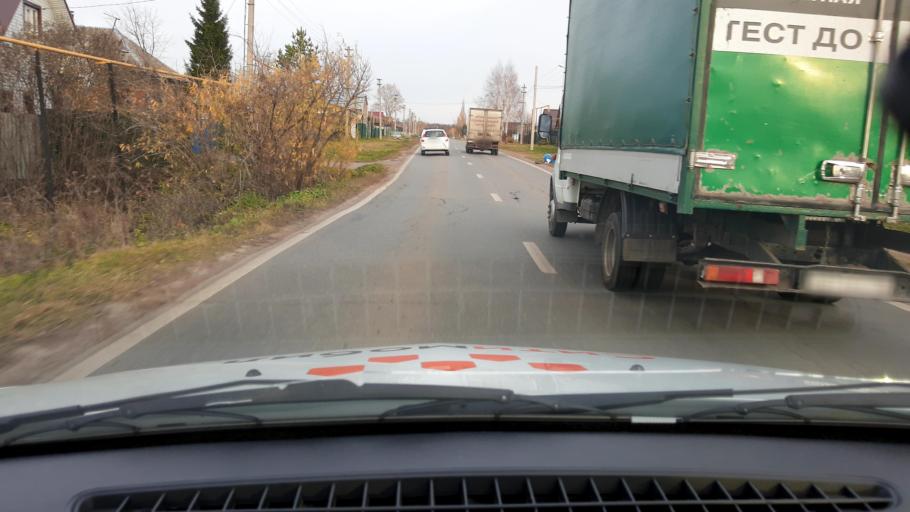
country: RU
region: Bashkortostan
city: Kabakovo
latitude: 54.7461
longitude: 56.2022
